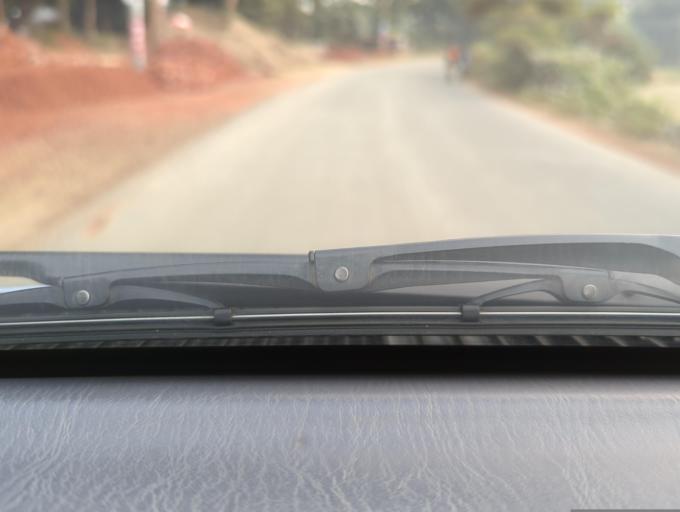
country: BD
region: Sylhet
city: Maulavi Bazar
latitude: 24.5037
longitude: 91.7358
